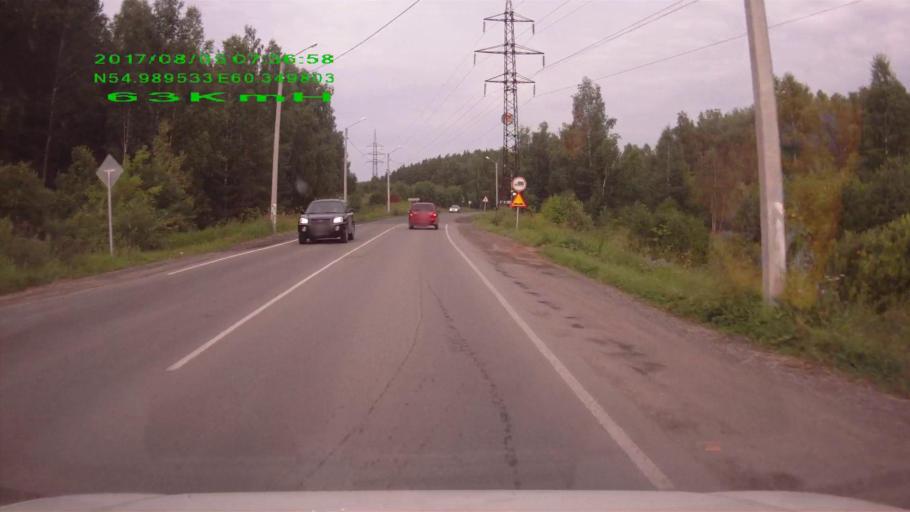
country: RU
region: Chelyabinsk
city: Chebarkul'
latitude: 54.9896
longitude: 60.3494
